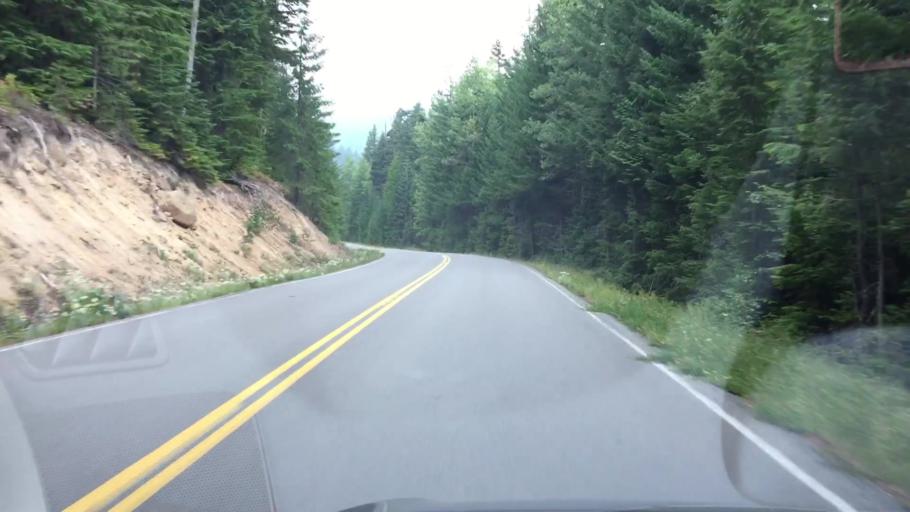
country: US
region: Washington
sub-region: Klickitat County
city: White Salmon
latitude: 46.1202
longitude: -121.6219
